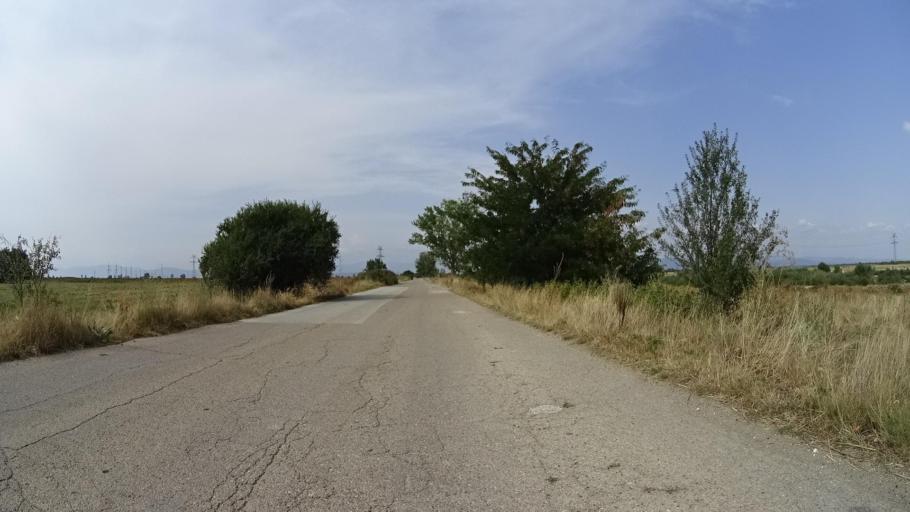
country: BG
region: Plovdiv
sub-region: Obshtina Kaloyanovo
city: Kaloyanovo
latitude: 42.3185
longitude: 24.7992
